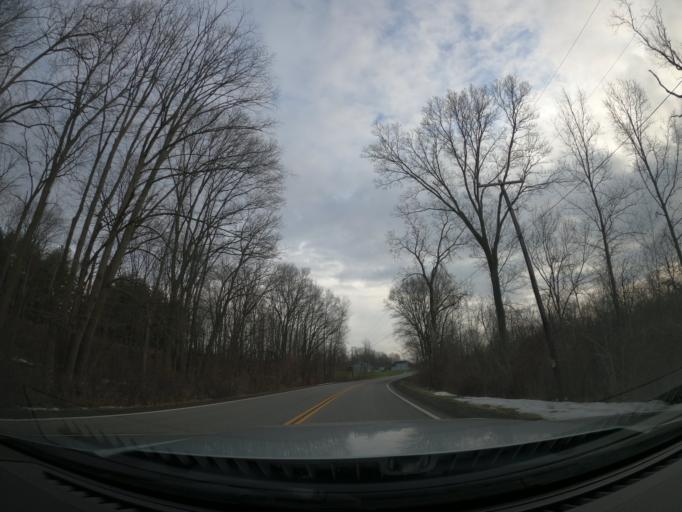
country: US
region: New York
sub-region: Yates County
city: Dundee
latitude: 42.5117
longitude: -76.9641
